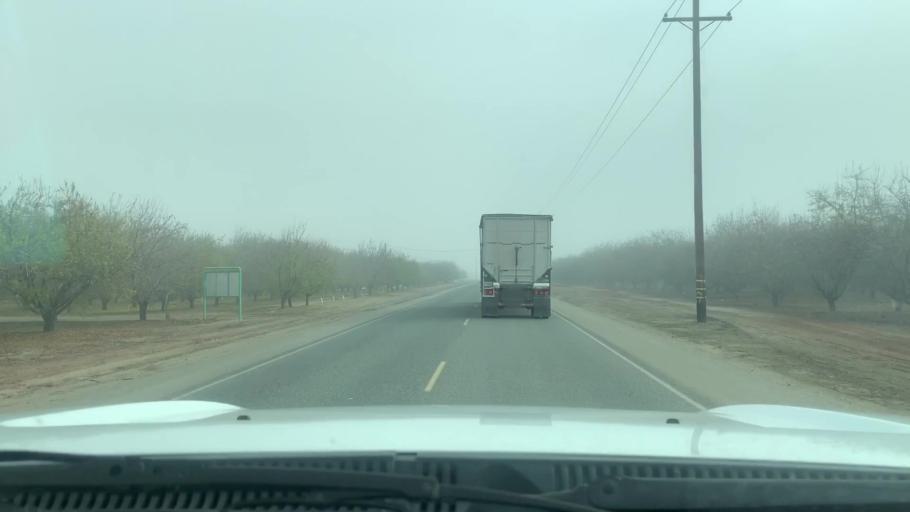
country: US
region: California
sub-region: Kern County
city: Buttonwillow
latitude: 35.5007
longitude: -119.5142
